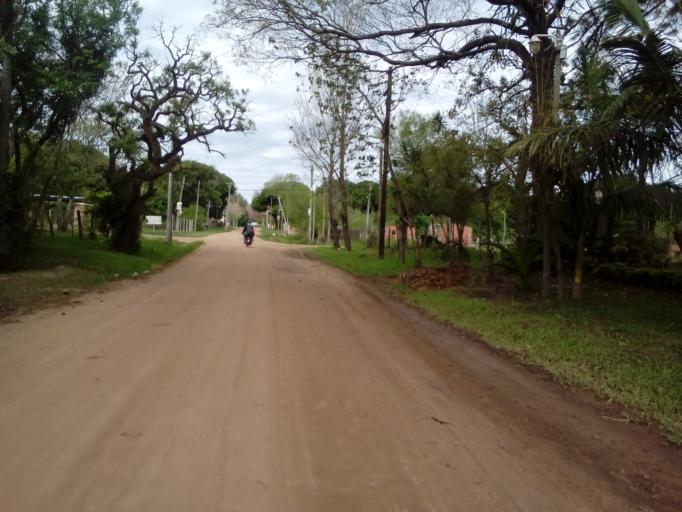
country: AR
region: Corrientes
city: San Luis del Palmar
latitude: -27.4580
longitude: -58.6553
